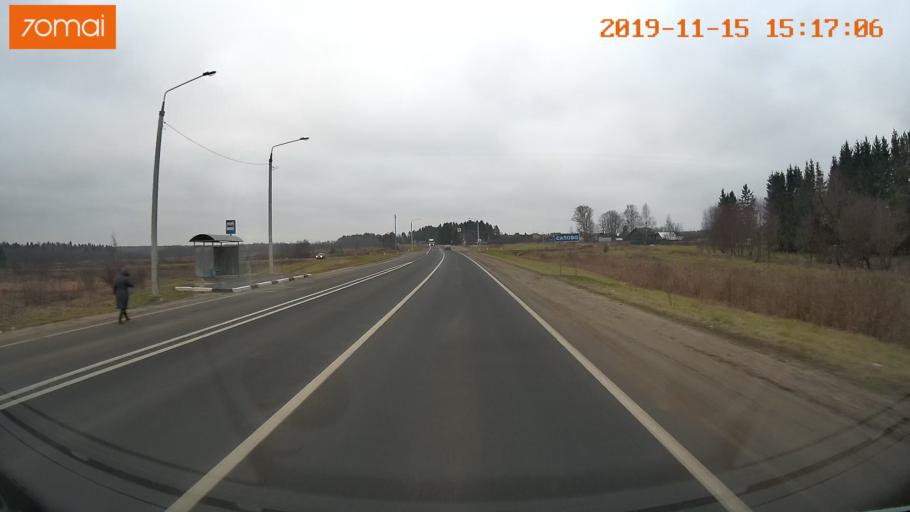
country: RU
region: Jaroslavl
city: Danilov
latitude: 58.2659
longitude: 40.1843
